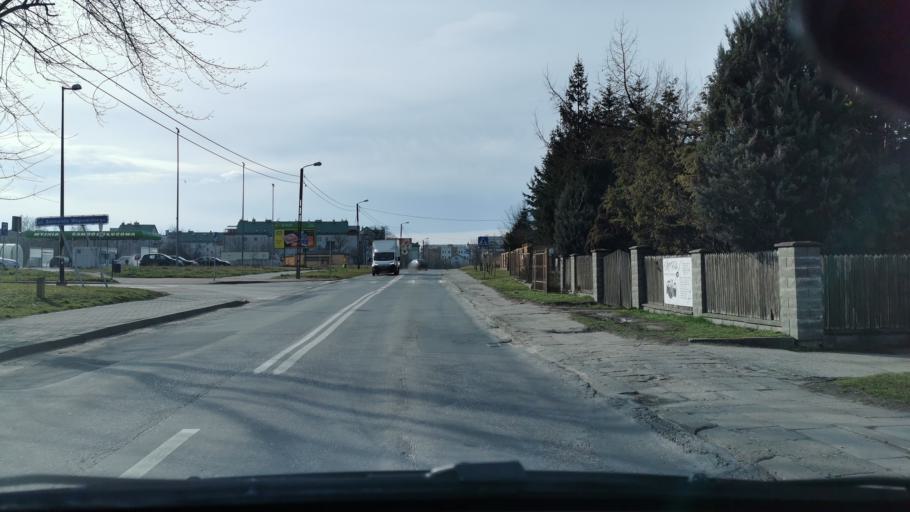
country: PL
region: Lublin Voivodeship
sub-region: Powiat lubelski
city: Lublin
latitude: 51.2035
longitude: 22.5434
